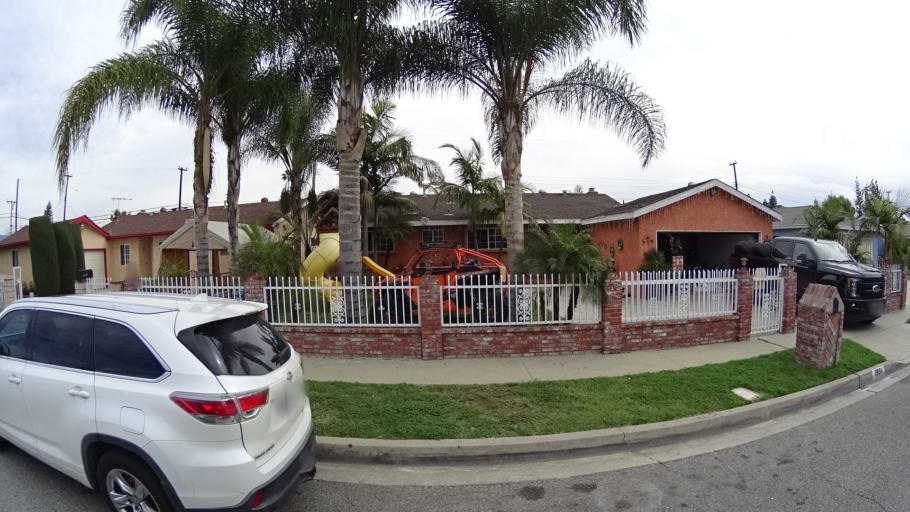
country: US
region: California
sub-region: Los Angeles County
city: Baldwin Park
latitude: 34.0834
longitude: -117.9819
